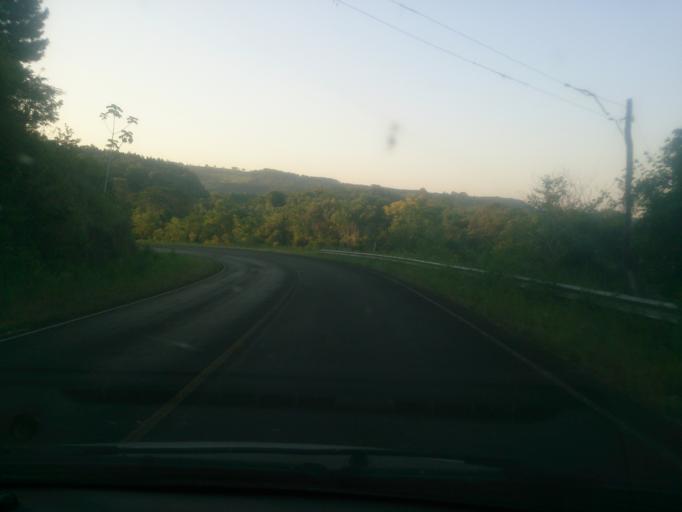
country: AR
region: Misiones
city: Panambi
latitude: -27.6780
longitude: -54.9082
